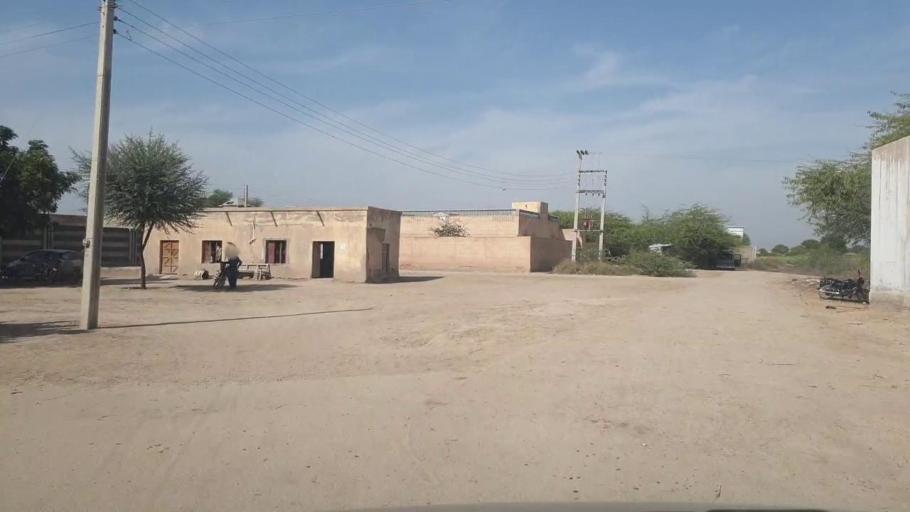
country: PK
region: Sindh
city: Kunri
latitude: 25.1862
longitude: 69.6743
